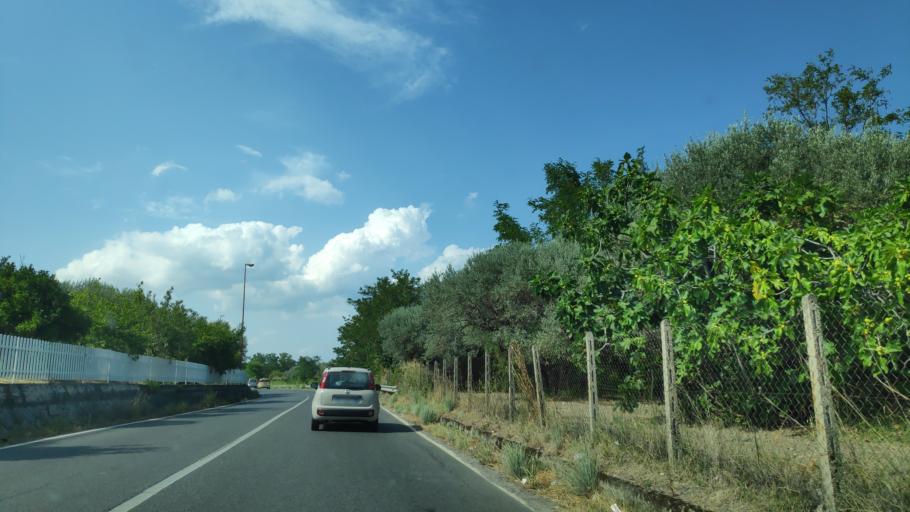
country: IT
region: Calabria
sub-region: Provincia di Catanzaro
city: Badolato Marina
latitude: 38.5840
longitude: 16.5646
